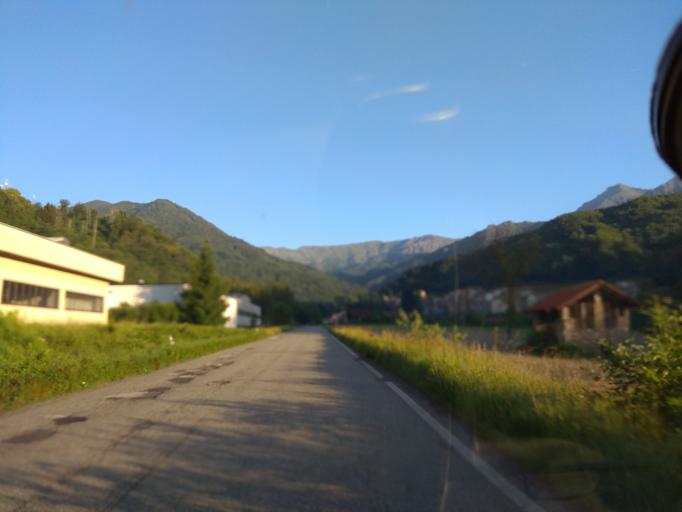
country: IT
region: Piedmont
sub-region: Provincia di Biella
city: Coggiola
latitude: 45.6801
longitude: 8.1923
